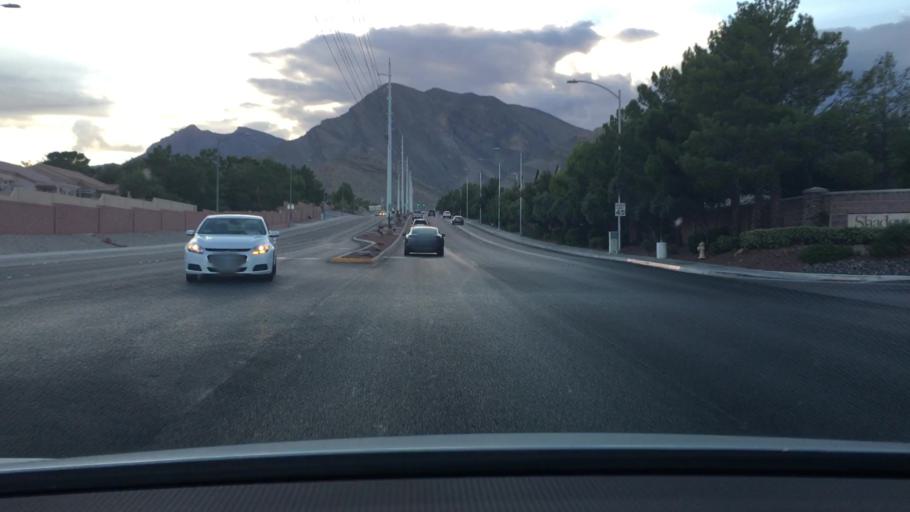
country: US
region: Nevada
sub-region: Clark County
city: Summerlin South
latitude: 36.2183
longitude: -115.3179
